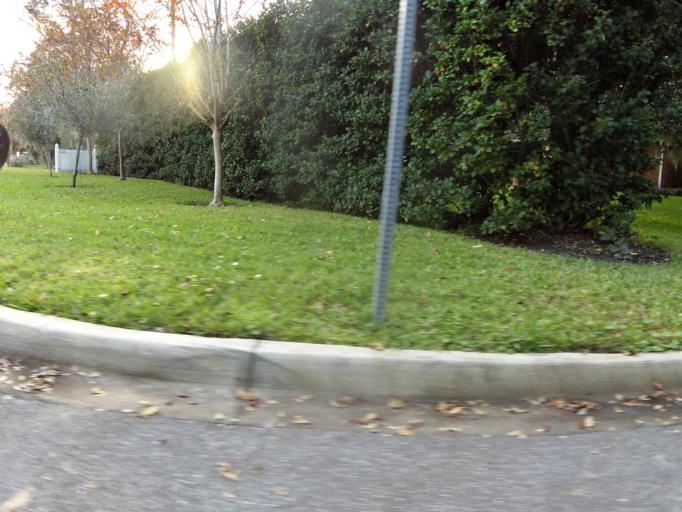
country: US
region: Florida
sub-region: Duval County
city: Jacksonville
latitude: 30.2896
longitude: -81.6540
